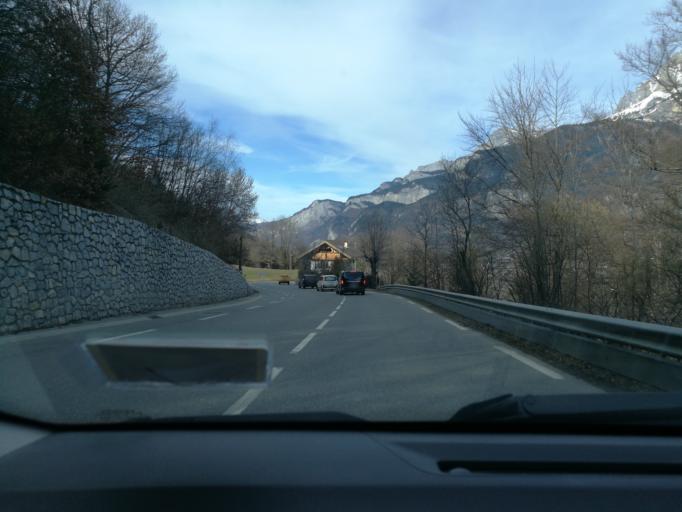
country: FR
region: Rhone-Alpes
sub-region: Departement de la Haute-Savoie
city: Domancy
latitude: 45.9188
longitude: 6.6355
